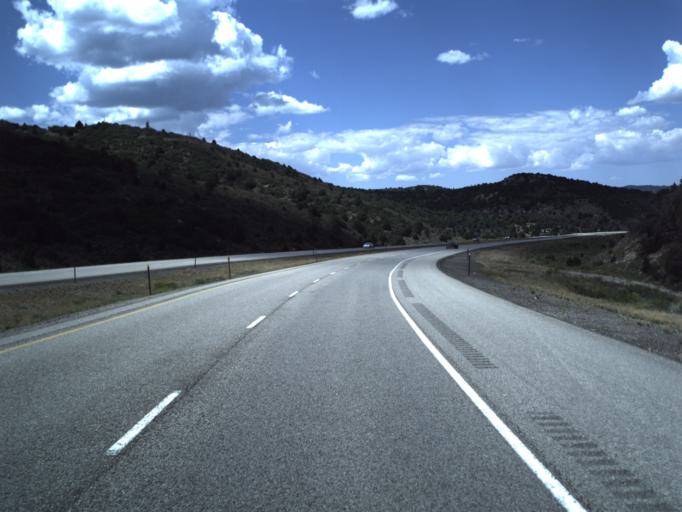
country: US
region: Utah
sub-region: Sevier County
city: Salina
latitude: 38.7839
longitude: -111.4945
